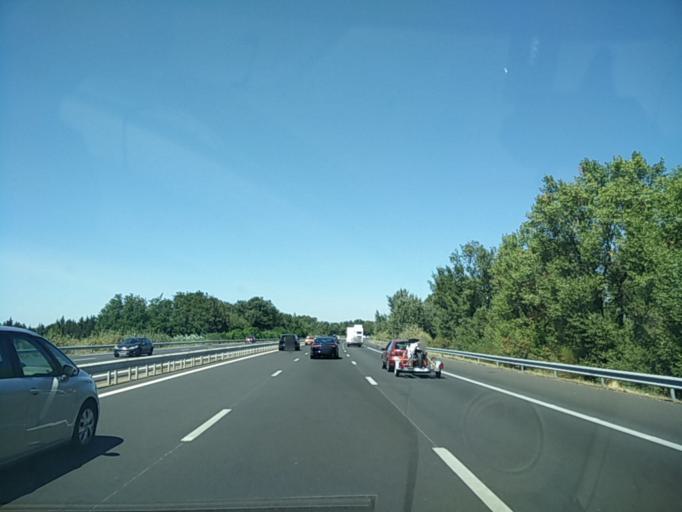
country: FR
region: Provence-Alpes-Cote d'Azur
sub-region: Departement des Bouches-du-Rhone
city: Cabannes
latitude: 43.8563
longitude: 4.9803
